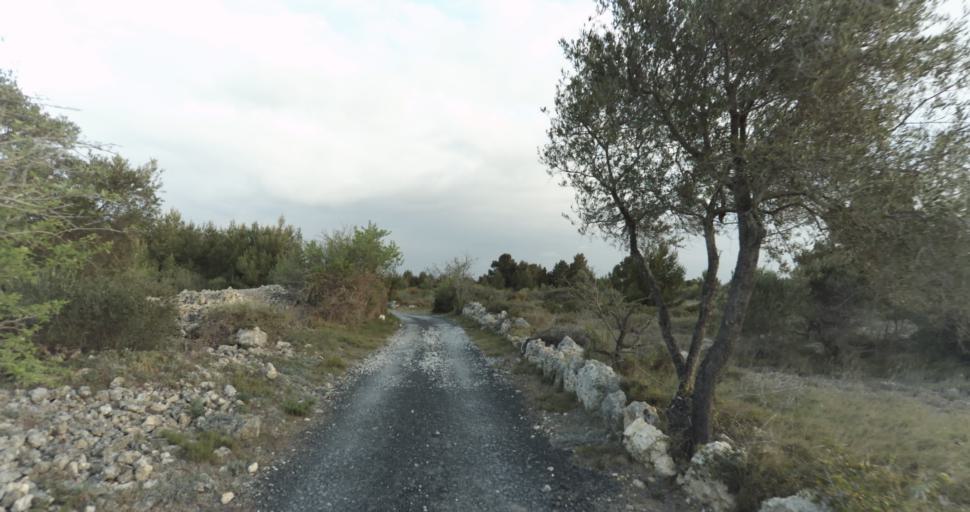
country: FR
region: Languedoc-Roussillon
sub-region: Departement de l'Aude
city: Leucate
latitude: 42.9218
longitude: 3.0208
